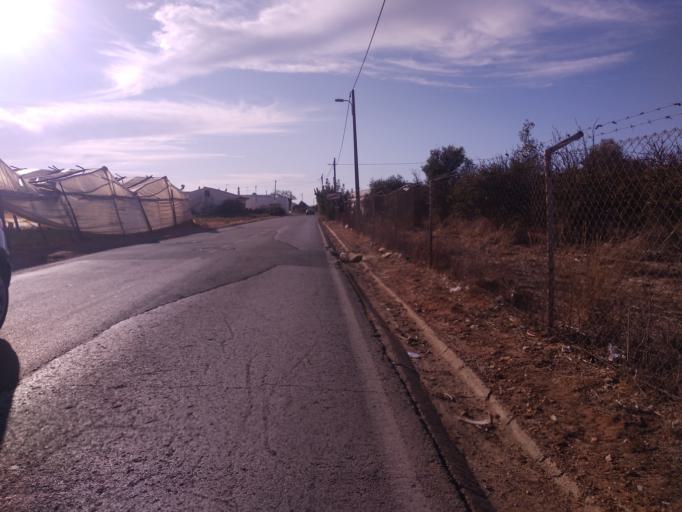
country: PT
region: Faro
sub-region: Faro
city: Faro
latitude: 37.0512
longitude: -7.9286
